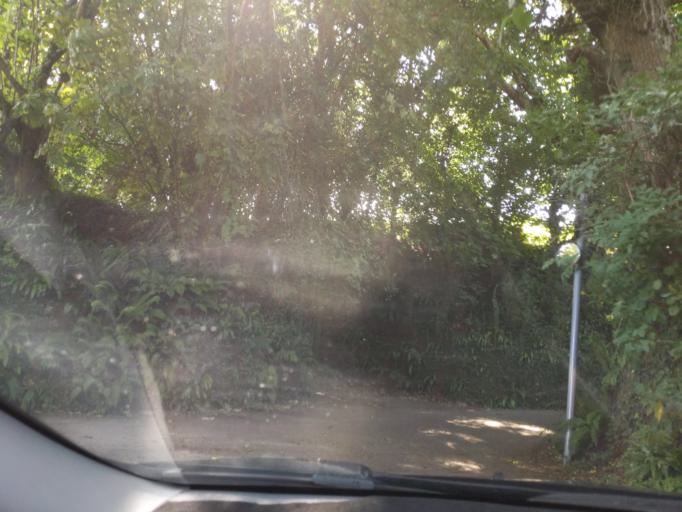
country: GB
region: England
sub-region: Devon
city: Plympton
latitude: 50.3789
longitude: -4.0501
